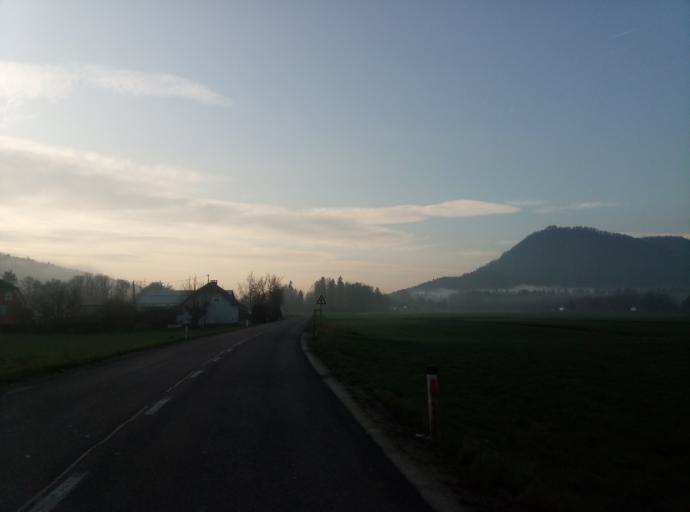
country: SI
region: Vodice
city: Vodice
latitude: 46.1485
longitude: 14.4807
